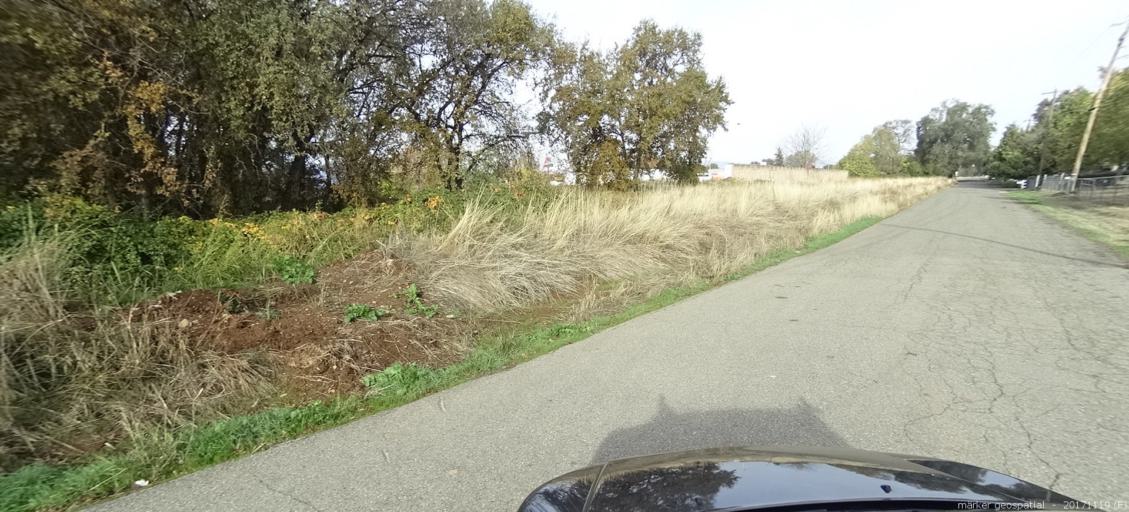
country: US
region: California
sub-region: Shasta County
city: Anderson
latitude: 40.5021
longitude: -122.3330
